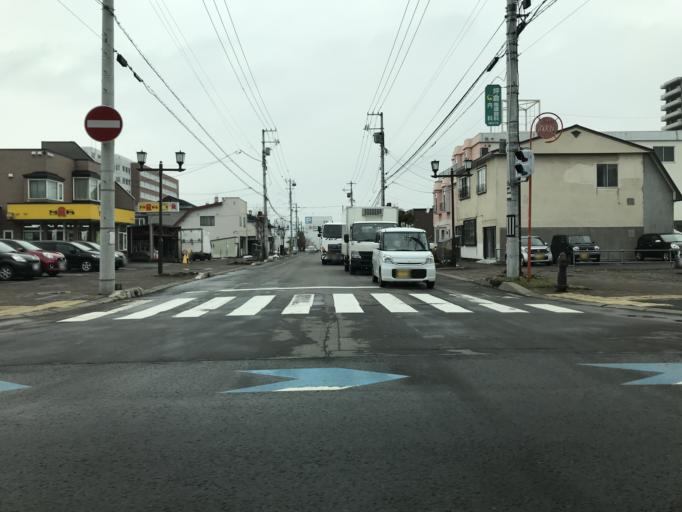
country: JP
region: Hokkaido
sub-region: Asahikawa-shi
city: Asahikawa
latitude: 43.7704
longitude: 142.3512
